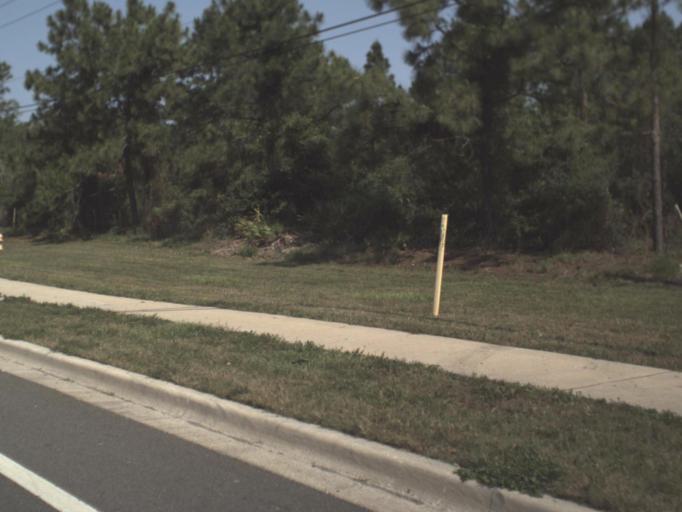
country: US
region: Florida
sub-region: Duval County
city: Neptune Beach
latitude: 30.2876
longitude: -81.4799
